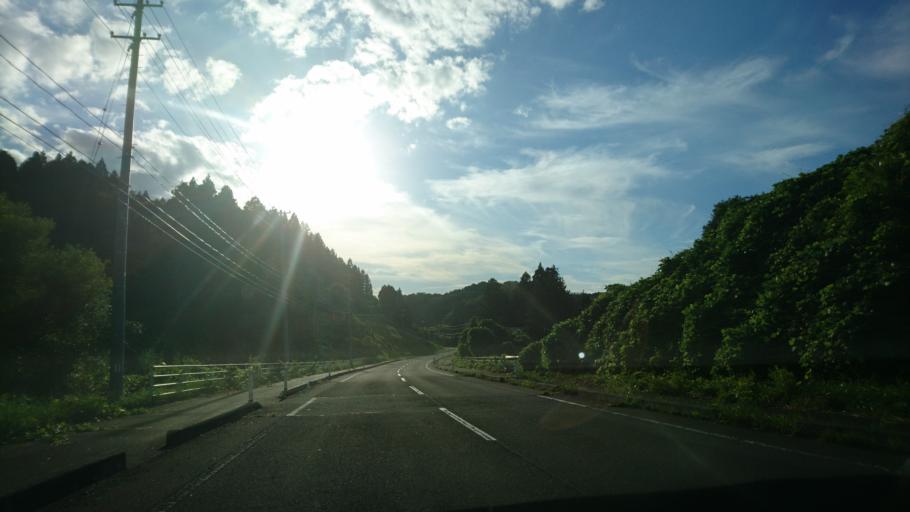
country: JP
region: Iwate
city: Ichinoseki
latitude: 38.8352
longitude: 141.0936
